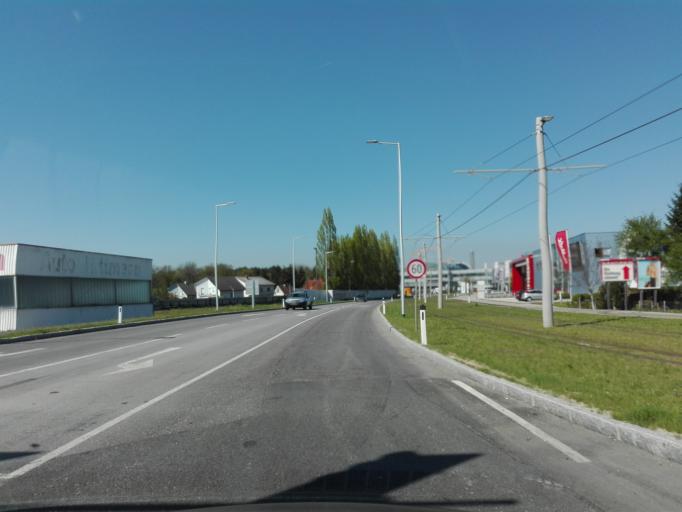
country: AT
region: Upper Austria
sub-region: Politischer Bezirk Linz-Land
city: Traun
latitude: 48.2382
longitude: 14.2346
